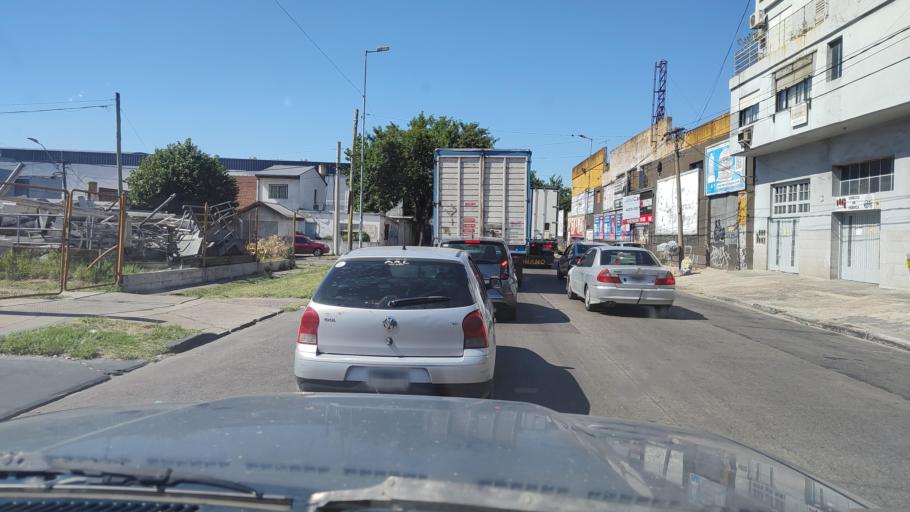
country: AR
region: Buenos Aires
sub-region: Partido de Moron
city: Moron
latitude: -34.6534
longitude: -58.6308
